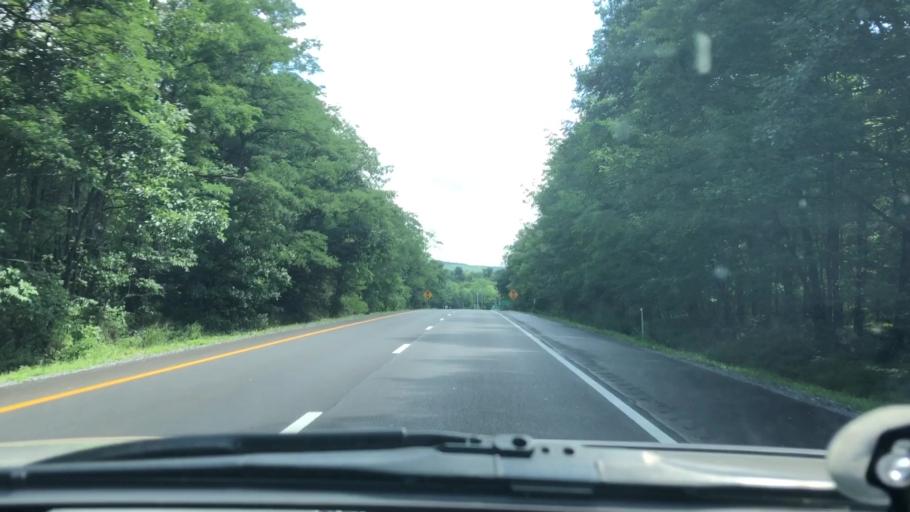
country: US
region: New York
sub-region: Greene County
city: Cairo
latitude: 42.3079
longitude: -74.0099
